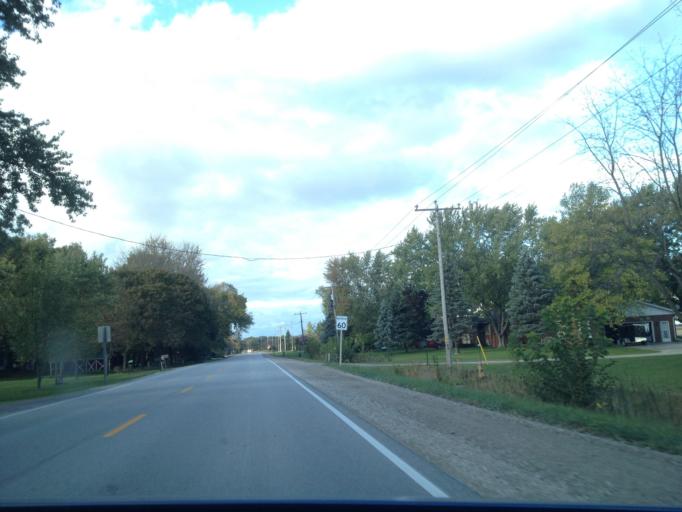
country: US
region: Michigan
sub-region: Wayne County
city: Grosse Pointe Farms
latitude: 42.2458
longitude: -82.7127
